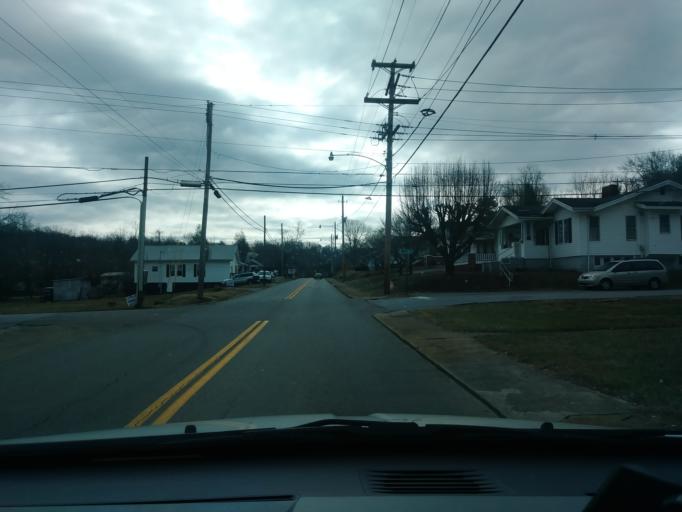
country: US
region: Tennessee
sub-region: Greene County
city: Greeneville
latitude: 36.1583
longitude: -82.8286
